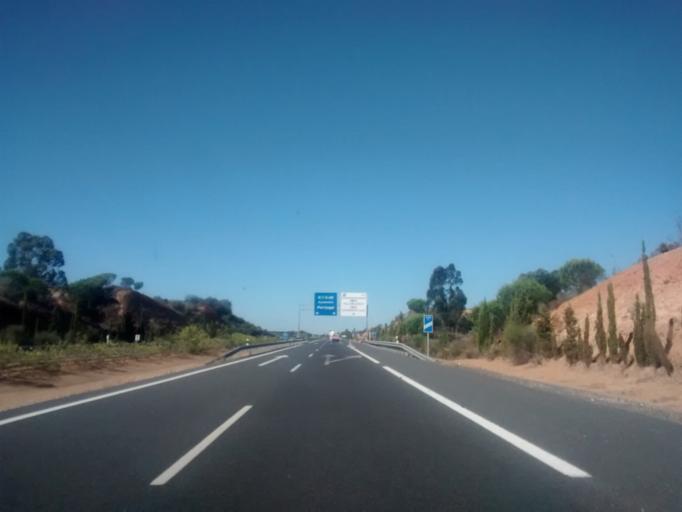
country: ES
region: Andalusia
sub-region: Provincia de Huelva
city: Villablanca
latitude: 37.2538
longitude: -7.3318
